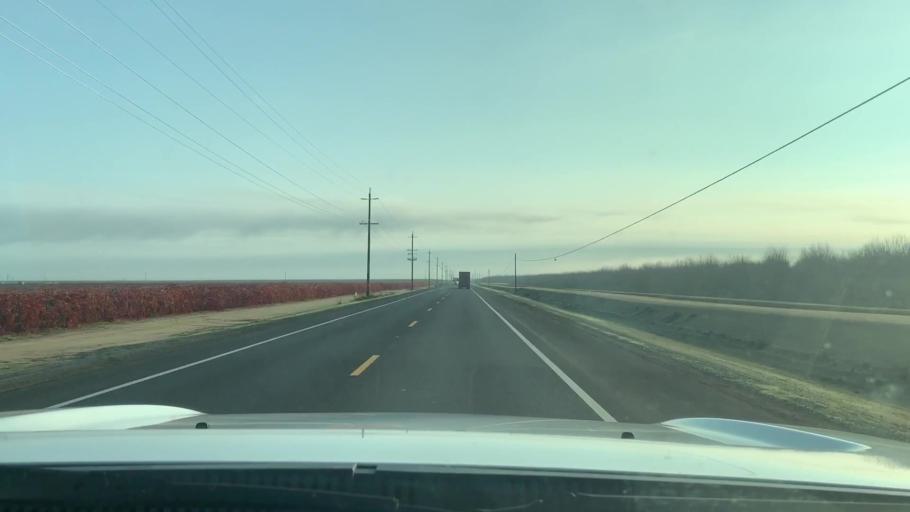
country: US
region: California
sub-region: Kern County
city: Wasco
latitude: 35.6018
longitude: -119.2704
